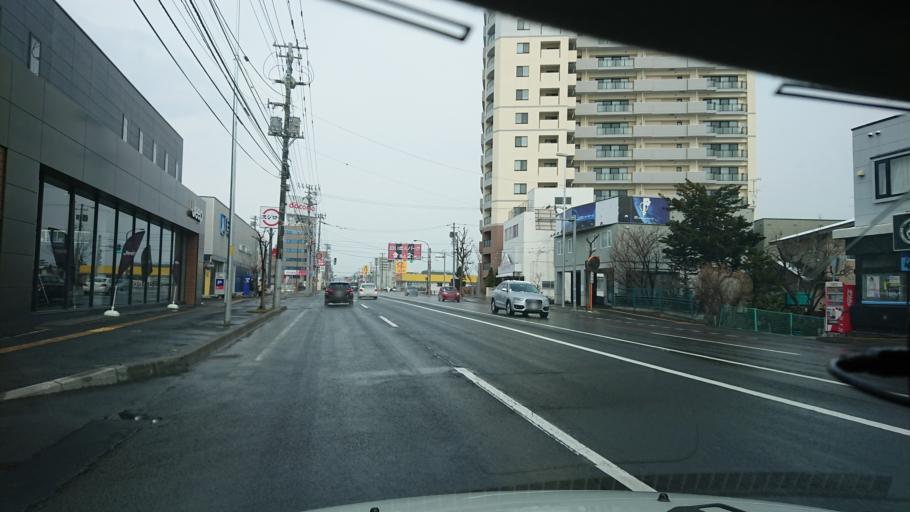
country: JP
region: Hokkaido
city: Sapporo
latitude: 43.0753
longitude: 141.2949
